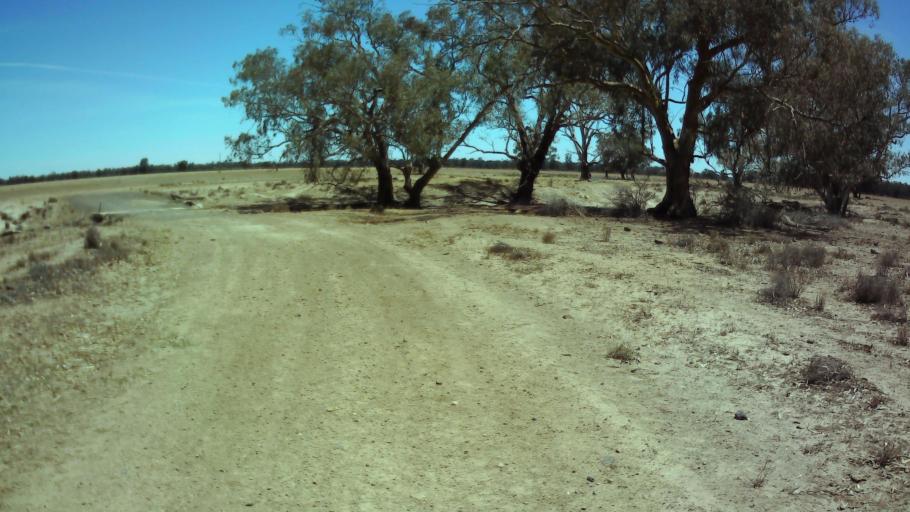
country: AU
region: New South Wales
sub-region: Bland
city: West Wyalong
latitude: -33.8366
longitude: 147.6330
